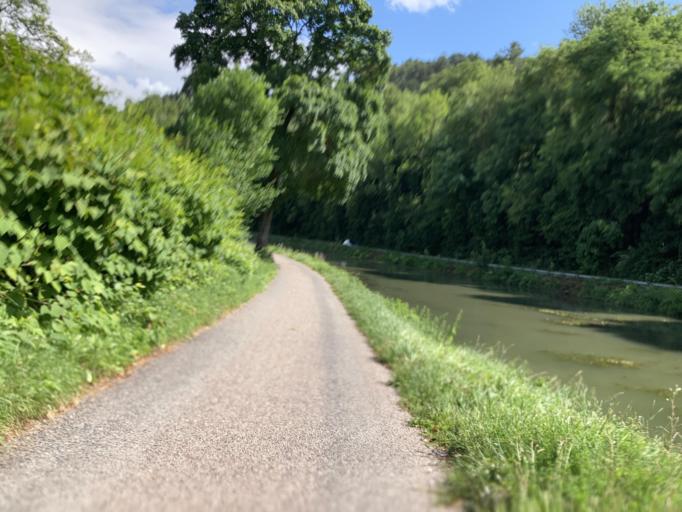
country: FR
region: Bourgogne
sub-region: Departement de la Cote-d'Or
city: Plombieres-les-Dijon
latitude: 47.3295
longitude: 4.9832
